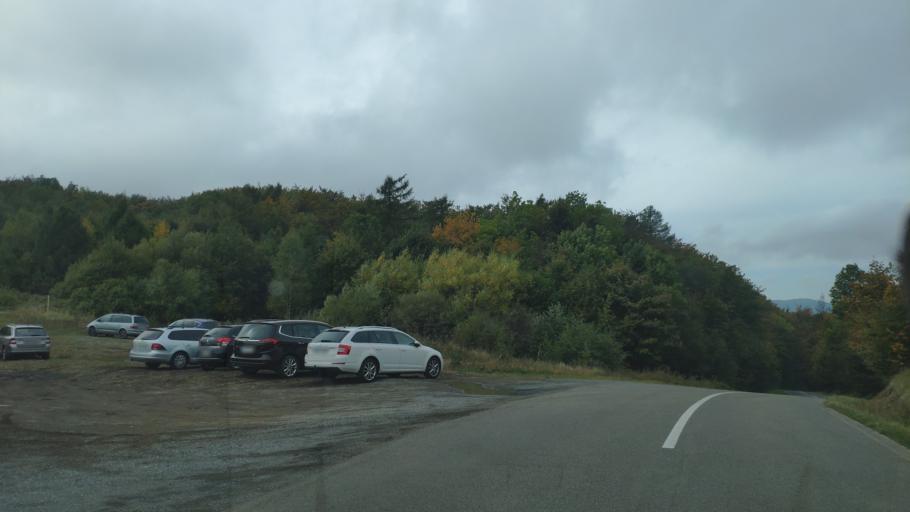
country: SK
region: Presovsky
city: Giraltovce
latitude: 48.9394
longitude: 21.4335
